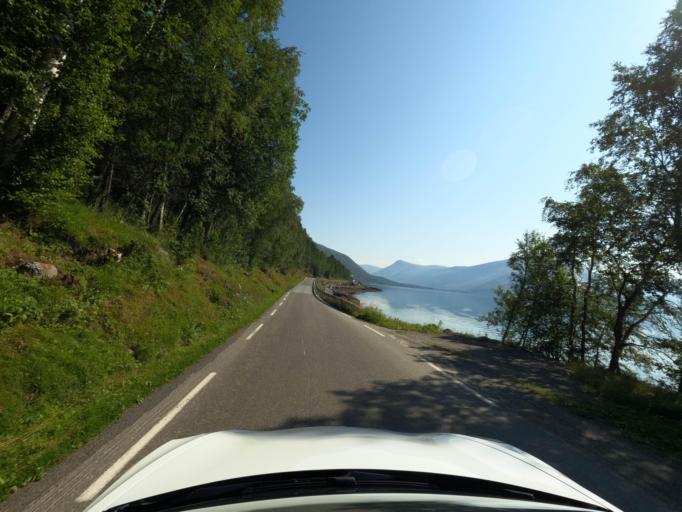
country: NO
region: Nordland
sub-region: Narvik
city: Narvik
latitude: 68.2886
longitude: 17.3655
